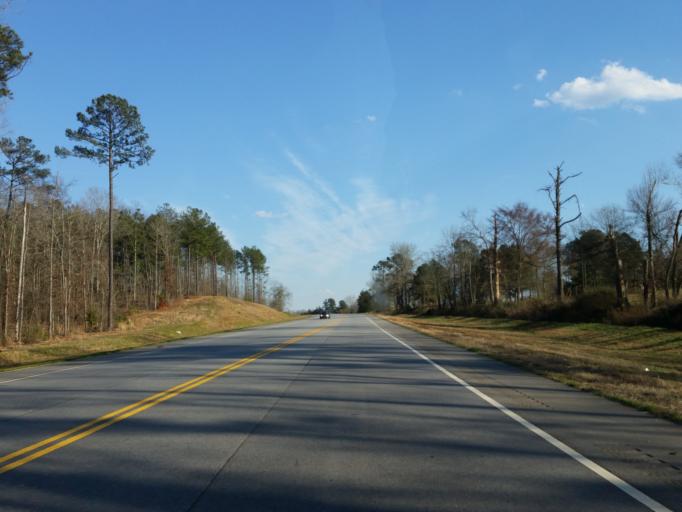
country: US
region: Georgia
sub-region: Monroe County
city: Forsyth
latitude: 33.0330
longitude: -83.9910
